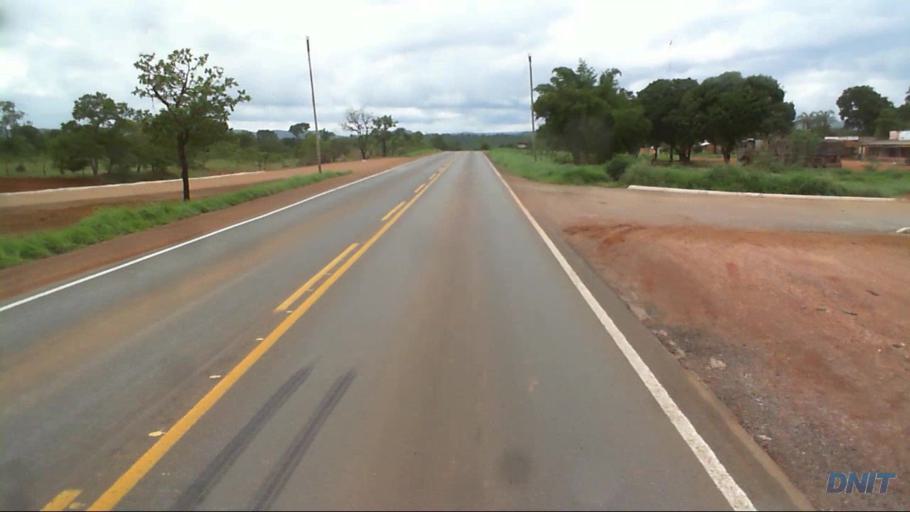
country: BR
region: Goias
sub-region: Padre Bernardo
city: Padre Bernardo
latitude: -15.3889
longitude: -48.2054
